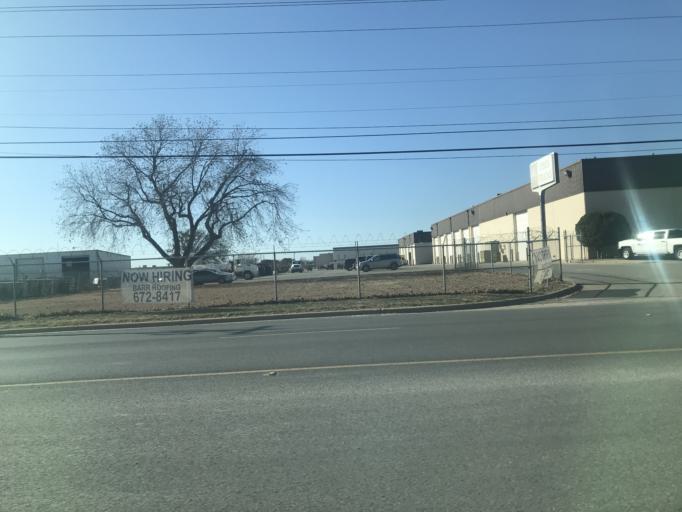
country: US
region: Texas
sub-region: Taylor County
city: Abilene
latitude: 32.4074
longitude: -99.7424
